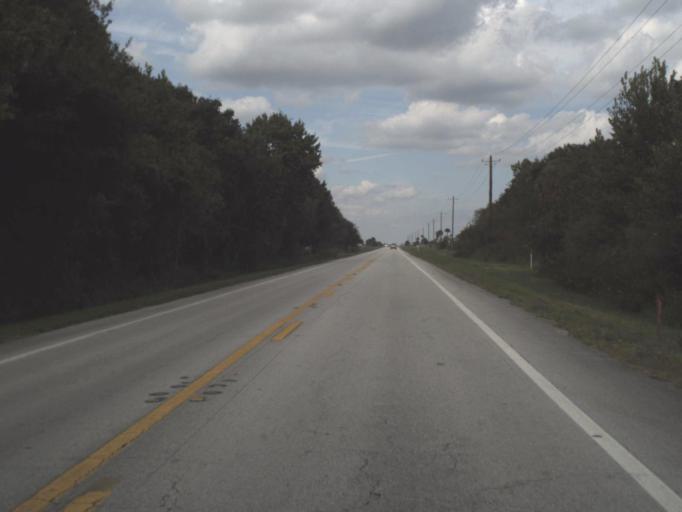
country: US
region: Florida
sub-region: Okeechobee County
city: Cypress Quarters
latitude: 27.4019
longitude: -80.8149
